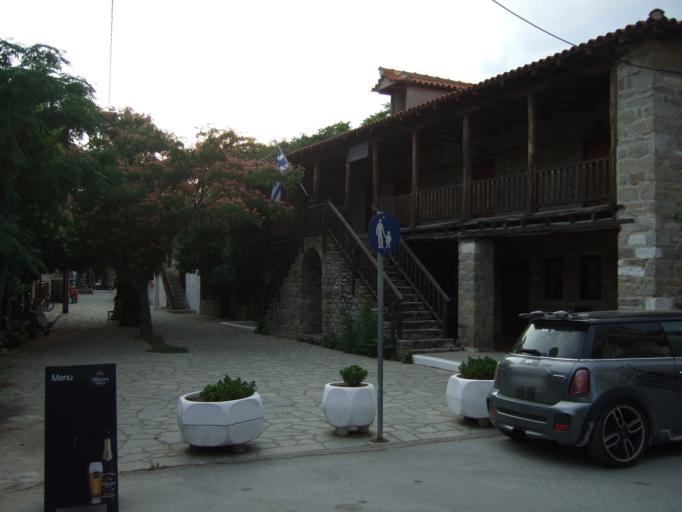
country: GR
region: Central Macedonia
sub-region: Nomos Chalkidikis
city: Ouranoupolis
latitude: 40.3252
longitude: 23.9810
